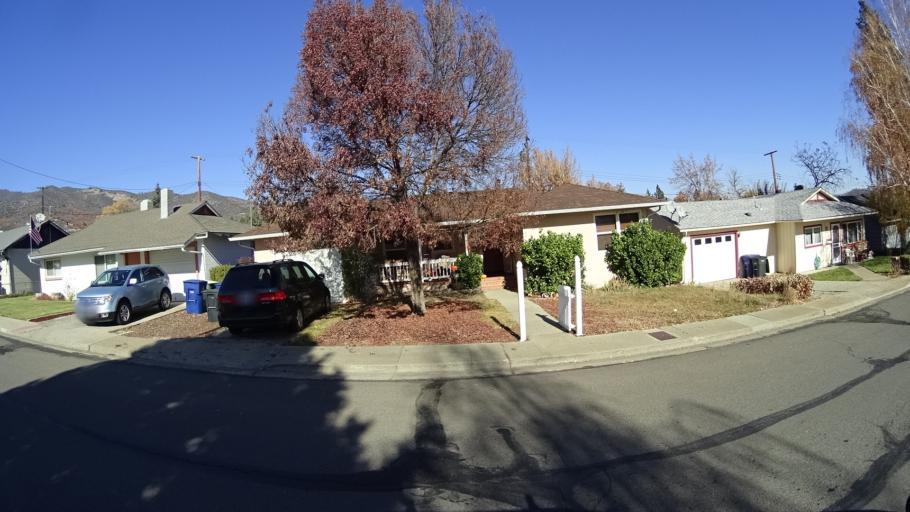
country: US
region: California
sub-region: Siskiyou County
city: Yreka
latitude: 41.7397
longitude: -122.6417
